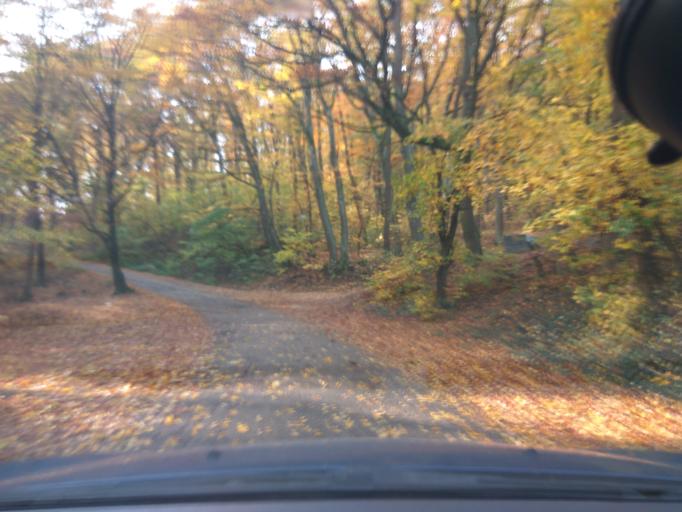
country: SK
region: Trnavsky
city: Vrbove
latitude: 48.6829
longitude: 17.7139
